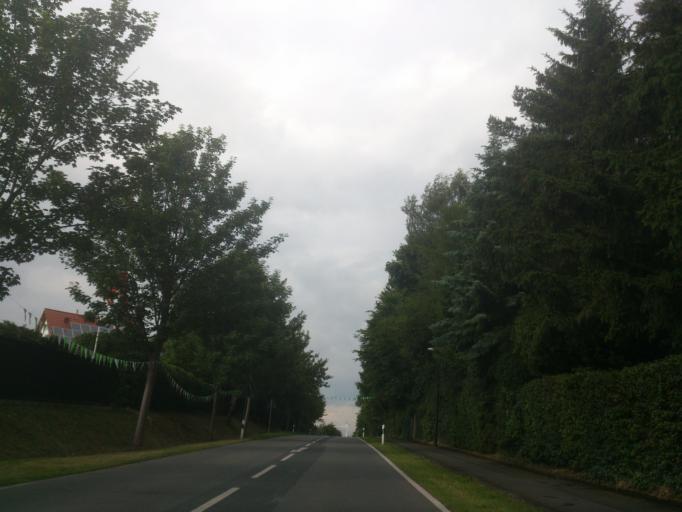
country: DE
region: North Rhine-Westphalia
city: Lichtenau
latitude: 51.6198
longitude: 8.9002
